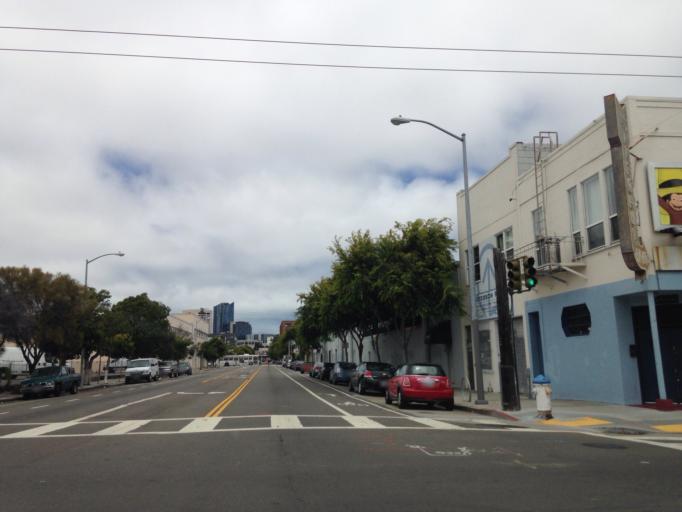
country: US
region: California
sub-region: San Francisco County
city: San Francisco
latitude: 37.7637
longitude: -122.4152
